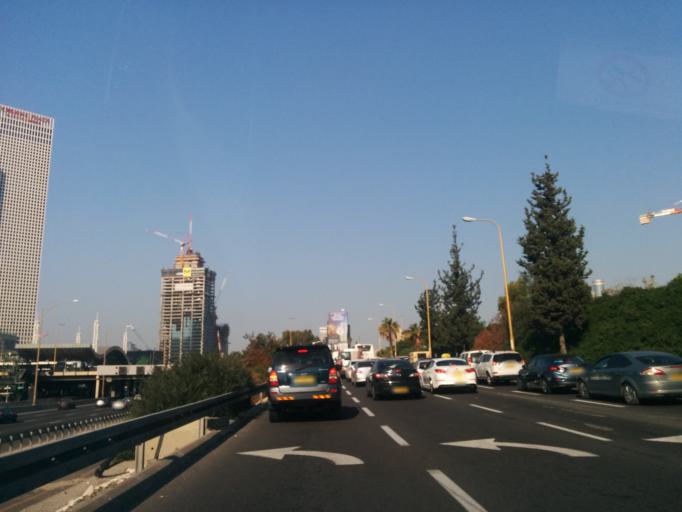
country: IL
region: Tel Aviv
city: Tel Aviv
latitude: 32.0711
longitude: 34.7937
